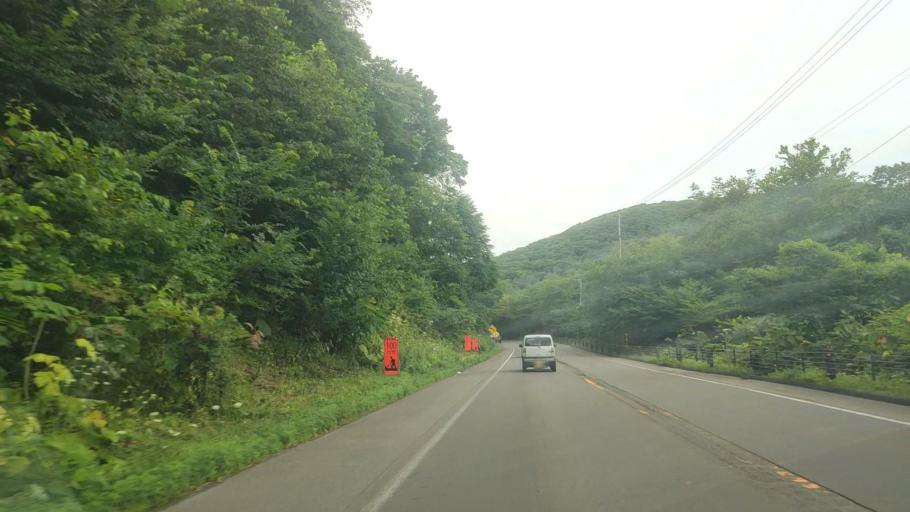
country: JP
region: Hokkaido
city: Nanae
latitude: 41.9735
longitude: 140.6469
